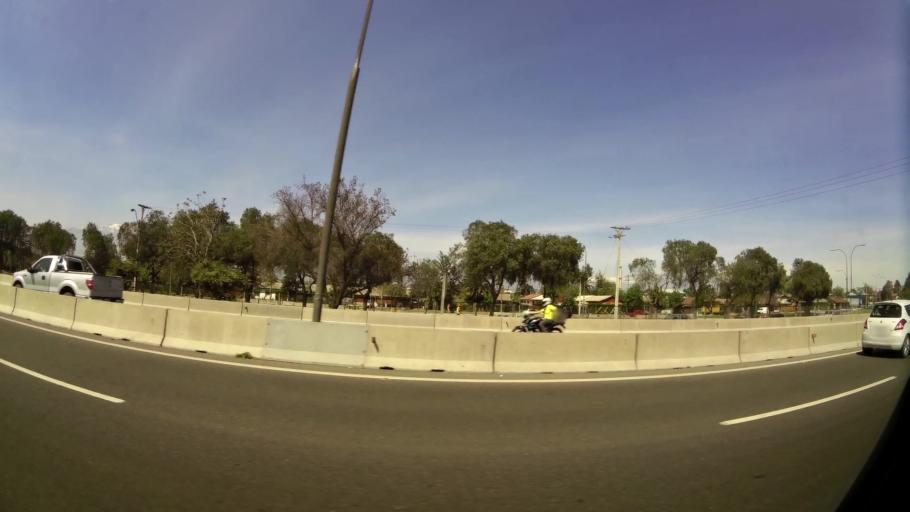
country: CL
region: Santiago Metropolitan
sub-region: Provincia de Maipo
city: San Bernardo
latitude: -33.5369
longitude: -70.6843
